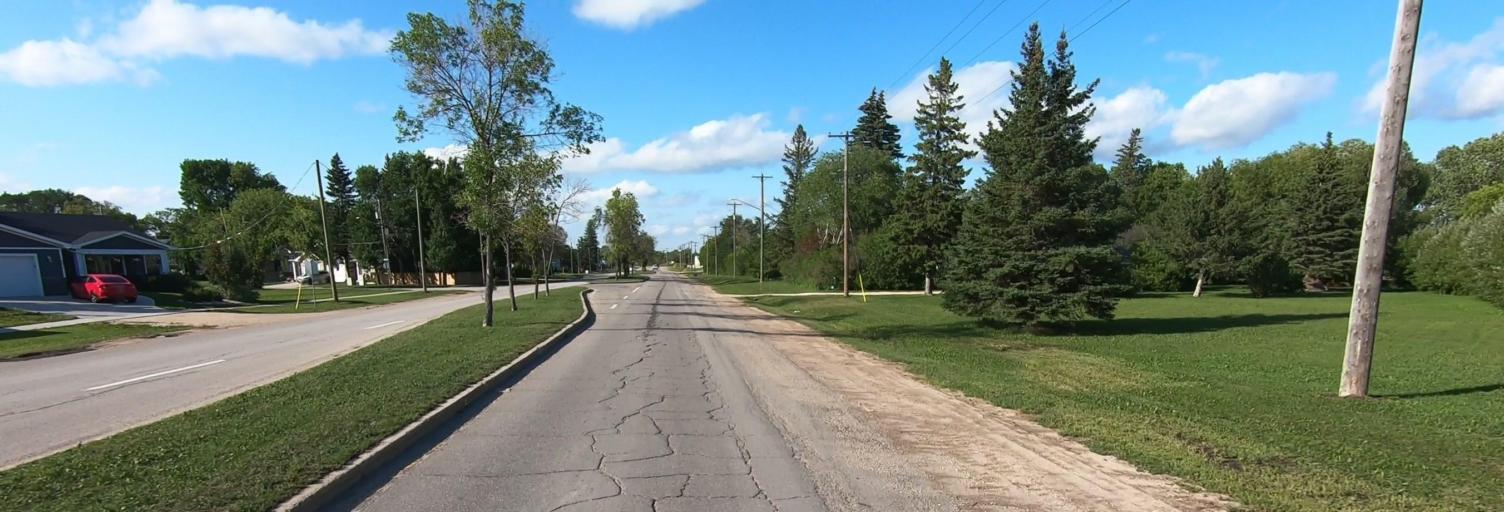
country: CA
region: Manitoba
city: Selkirk
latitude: 50.1502
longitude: -96.8670
